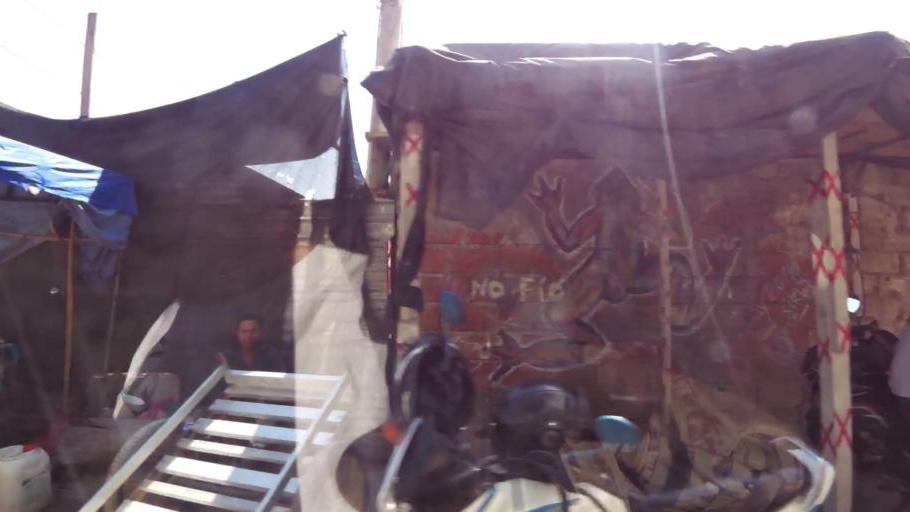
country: CO
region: Bolivar
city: Cartagena
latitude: 10.3869
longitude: -75.5113
